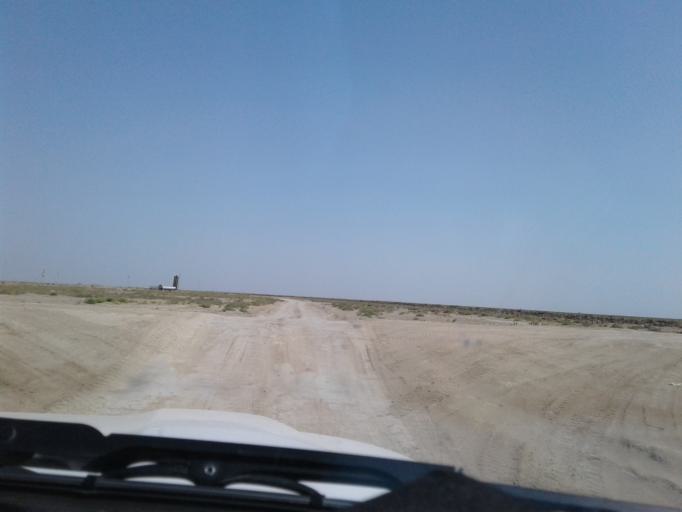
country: IR
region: Golestan
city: Gomishan
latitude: 37.8167
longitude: 53.9217
